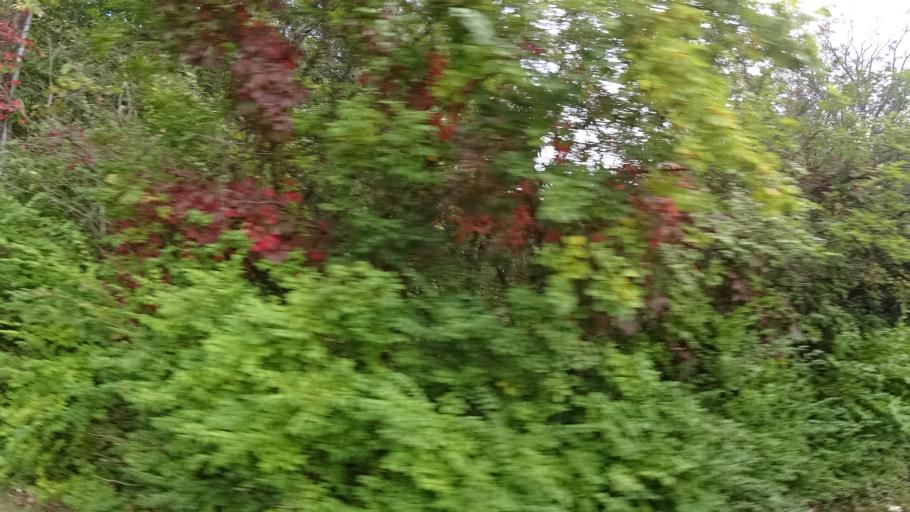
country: US
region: Indiana
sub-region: LaPorte County
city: Long Beach
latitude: 41.7188
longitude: -86.8407
